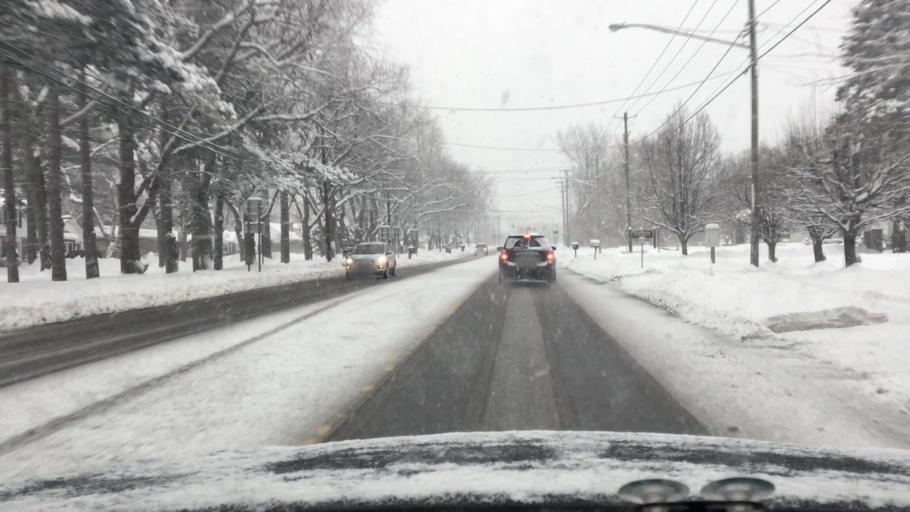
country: US
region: New York
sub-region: Erie County
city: Orchard Park
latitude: 42.7912
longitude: -78.7515
